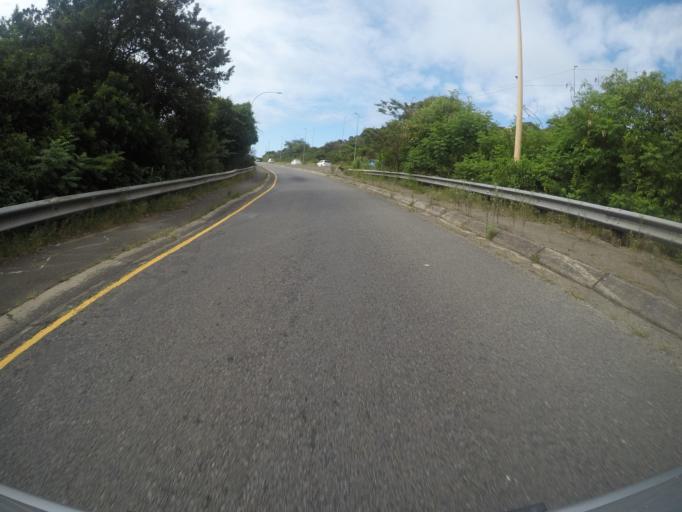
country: ZA
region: Eastern Cape
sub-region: Buffalo City Metropolitan Municipality
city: East London
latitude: -32.9770
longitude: 27.9199
